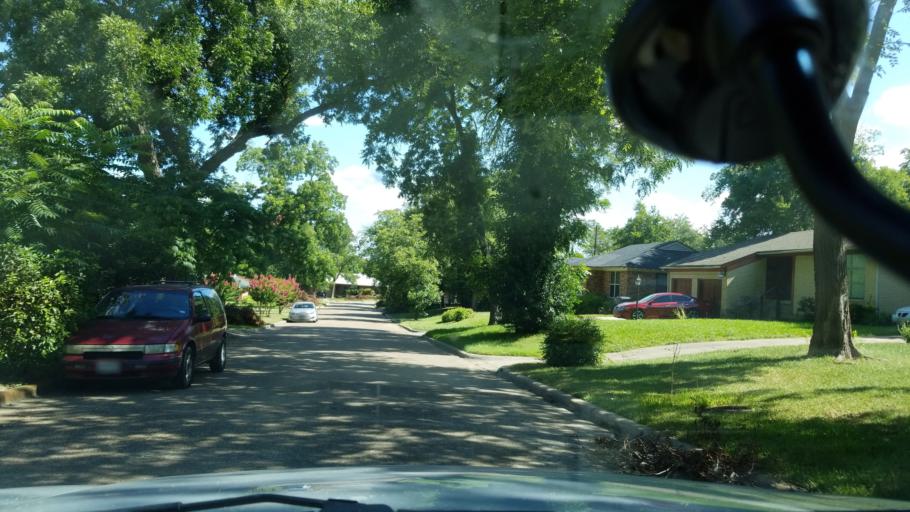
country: US
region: Texas
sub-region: Dallas County
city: Cockrell Hill
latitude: 32.6819
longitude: -96.8133
